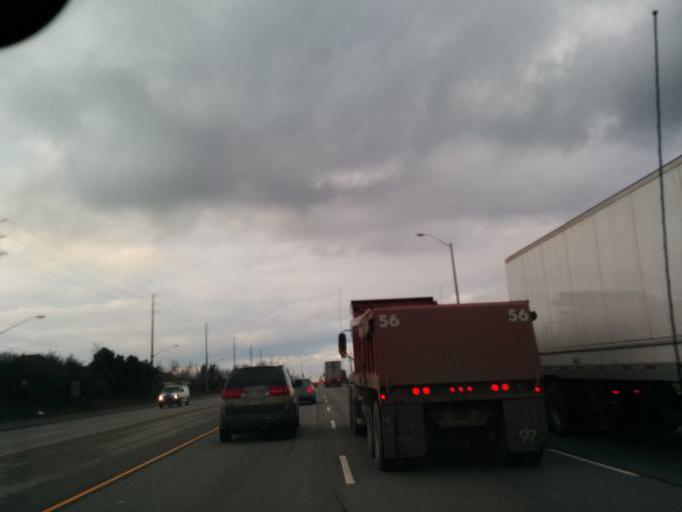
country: CA
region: Ontario
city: Brampton
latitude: 43.7821
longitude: -79.6569
